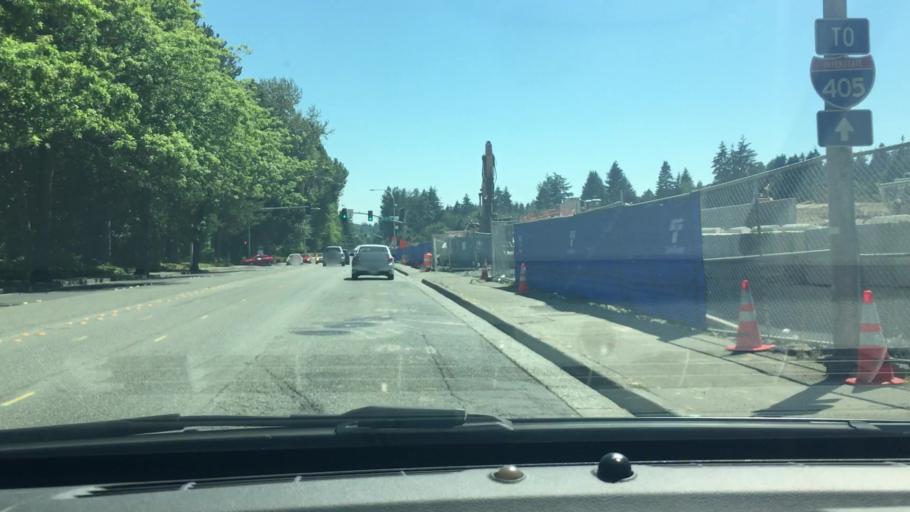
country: US
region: Washington
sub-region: King County
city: Bellevue
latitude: 47.6055
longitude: -122.1909
